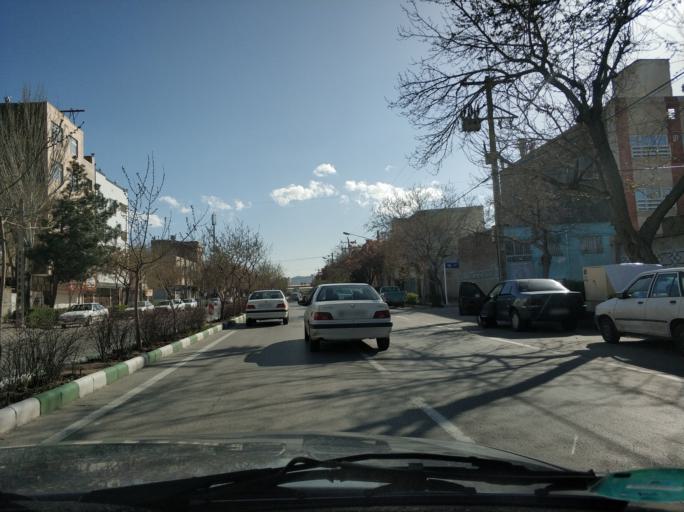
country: IR
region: Razavi Khorasan
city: Mashhad
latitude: 36.3131
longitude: 59.6255
